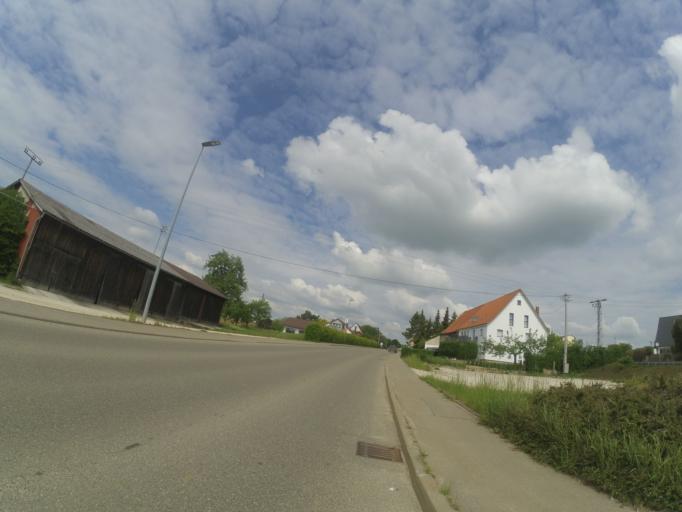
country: DE
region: Baden-Wuerttemberg
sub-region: Tuebingen Region
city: Berghulen
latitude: 48.4589
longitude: 9.7766
